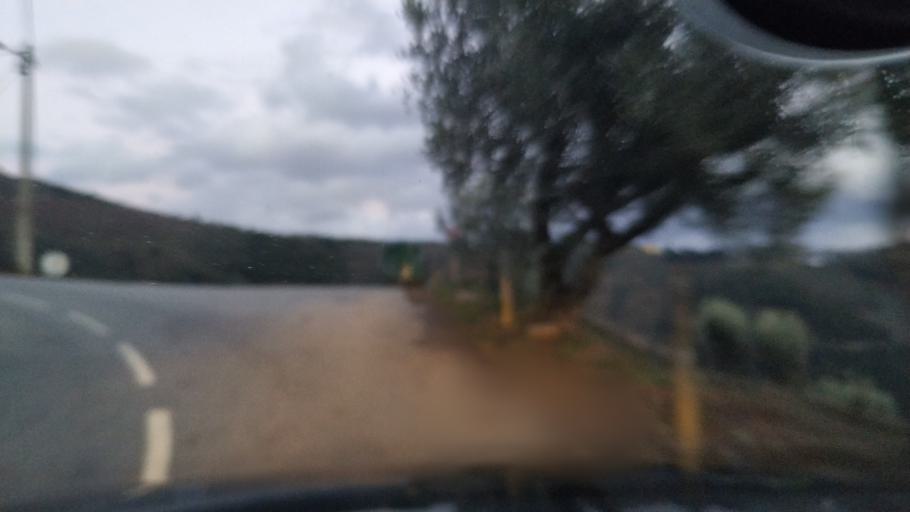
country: PT
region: Vila Real
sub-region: Santa Marta de Penaguiao
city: Santa Marta de Penaguiao
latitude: 41.2372
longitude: -7.7737
